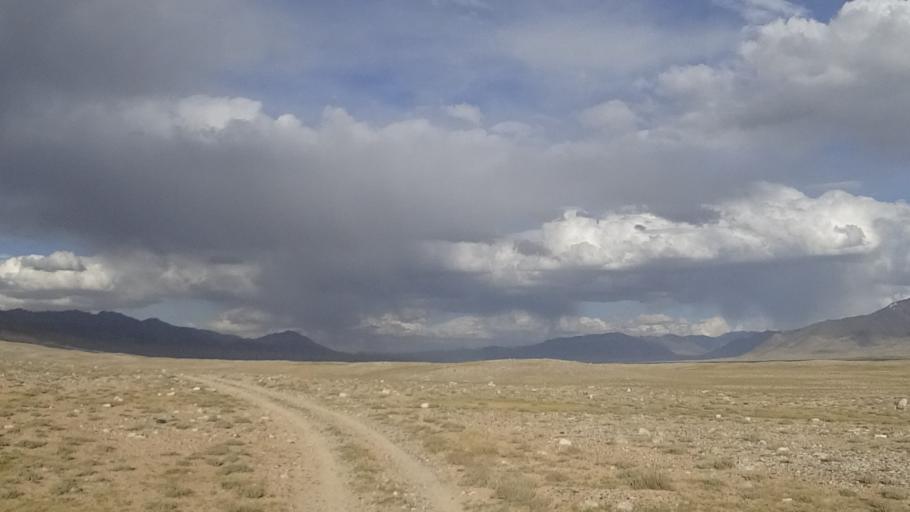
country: TJ
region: Gorno-Badakhshan
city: Murghob
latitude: 37.4617
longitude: 73.6170
